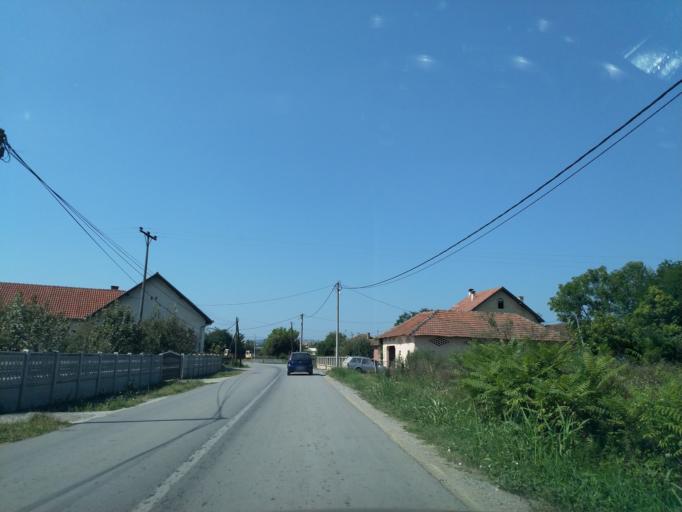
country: RS
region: Central Serbia
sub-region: Rasinski Okrug
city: Trstenik
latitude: 43.6266
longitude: 21.1439
